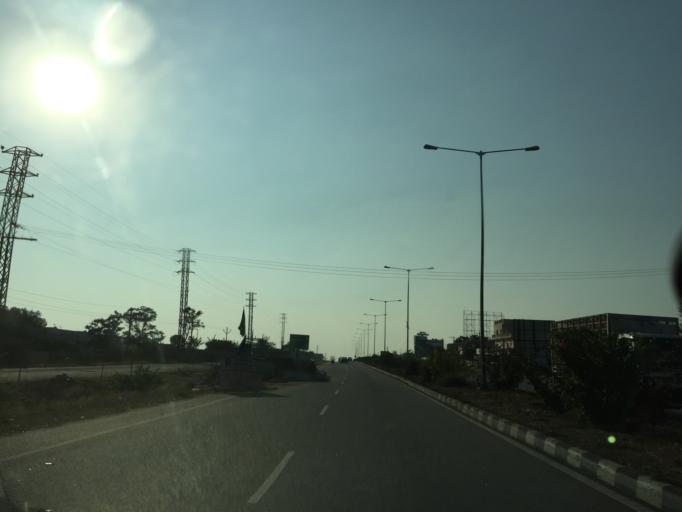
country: IN
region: Telangana
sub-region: Nalgonda
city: Bhongir
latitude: 17.5045
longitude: 78.8646
